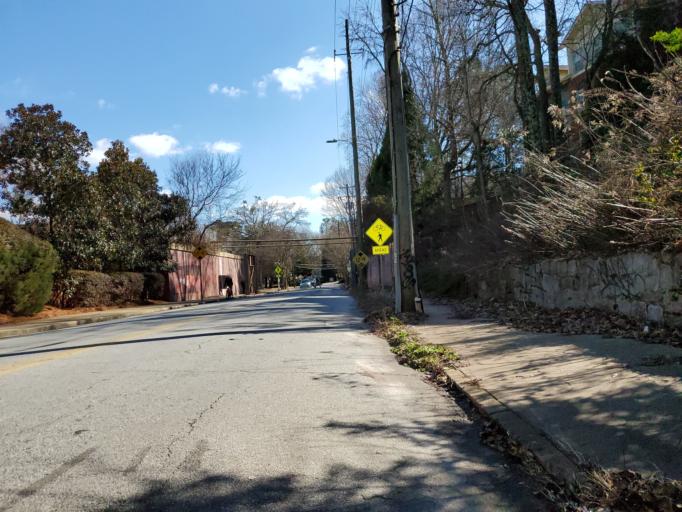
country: US
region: Georgia
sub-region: Fulton County
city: Atlanta
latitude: 33.7288
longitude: -84.3642
